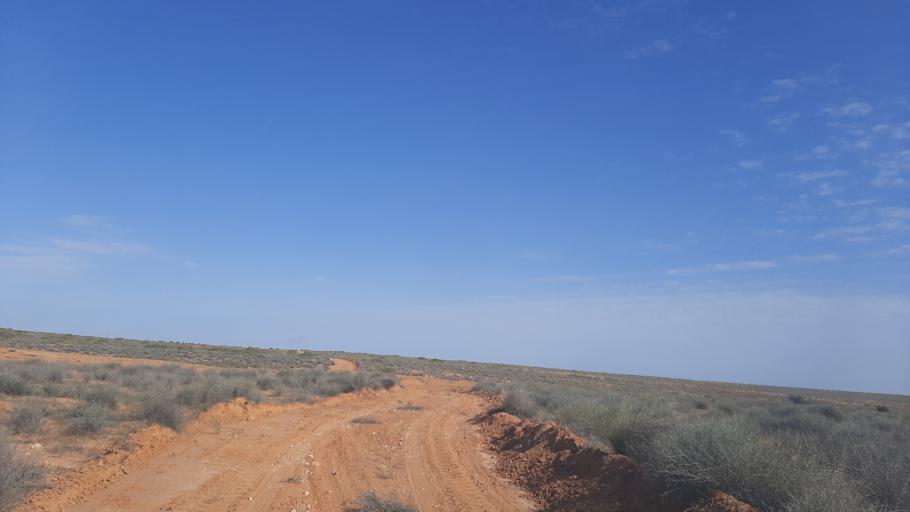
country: TN
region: Madanin
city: Medenine
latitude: 33.2468
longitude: 10.7451
